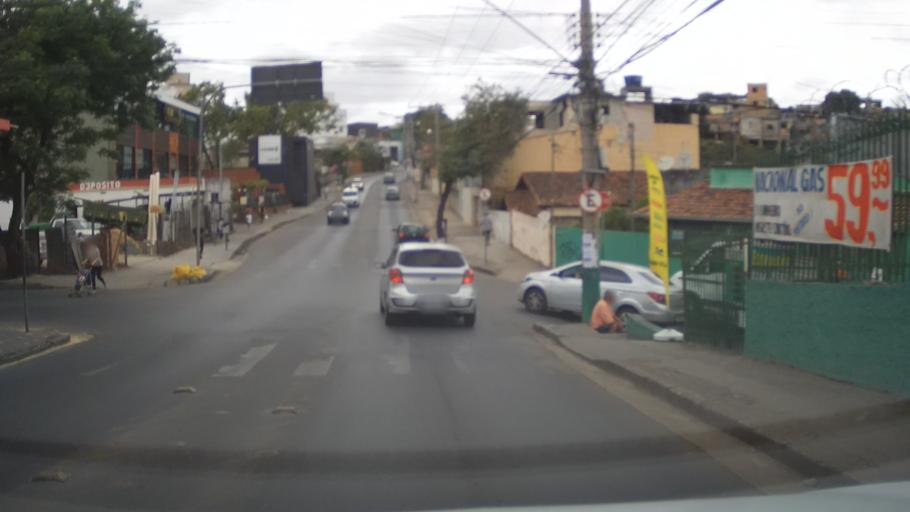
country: BR
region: Minas Gerais
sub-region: Belo Horizonte
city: Belo Horizonte
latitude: -19.8468
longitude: -43.9401
